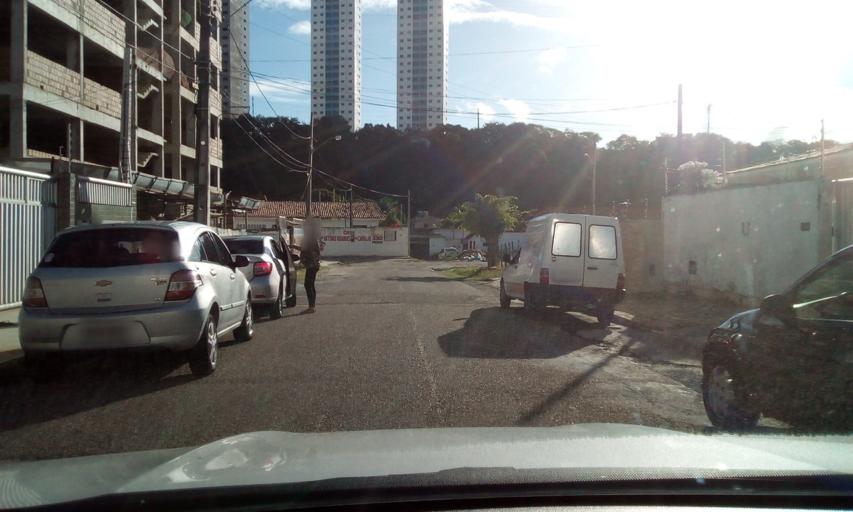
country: BR
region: Paraiba
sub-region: Joao Pessoa
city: Joao Pessoa
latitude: -7.1053
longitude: -34.8406
